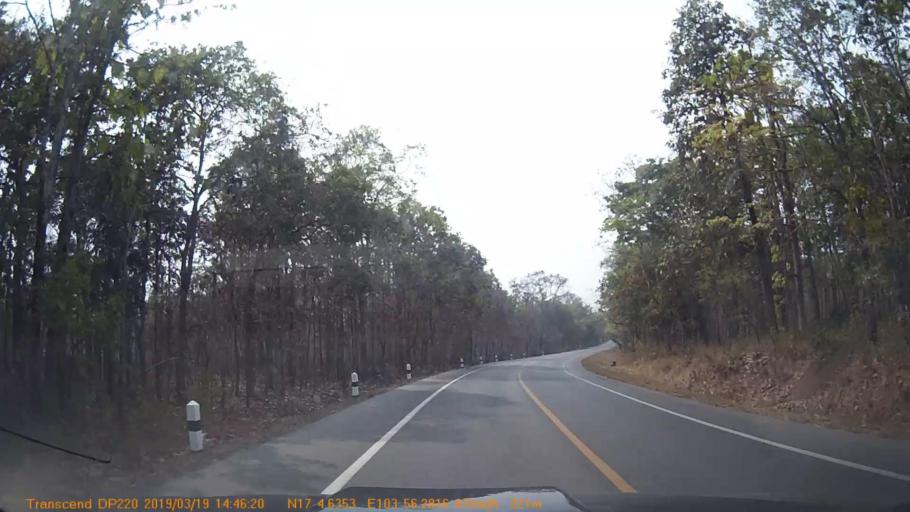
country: TH
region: Sakon Nakhon
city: Phu Phan
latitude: 17.0774
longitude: 103.9378
